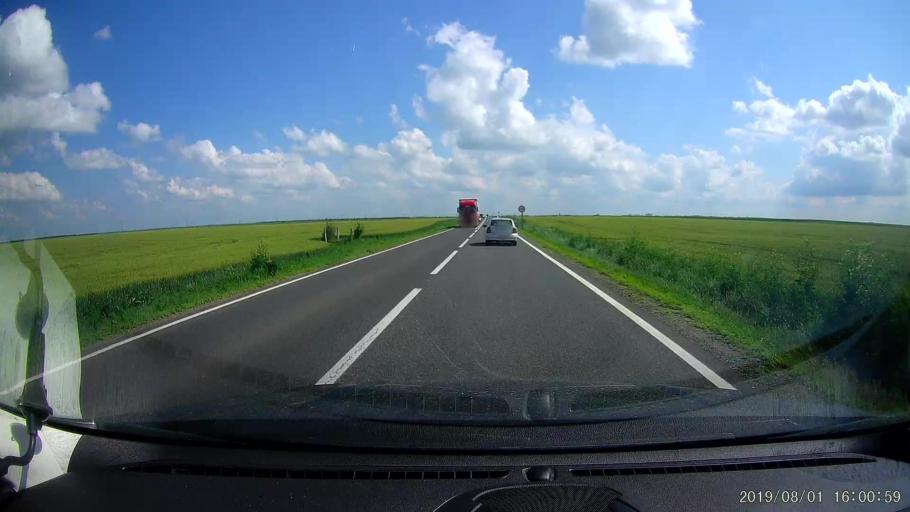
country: RO
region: Ialomita
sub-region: Comuna Ciulnita
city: Ciulnita
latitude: 44.5164
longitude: 27.3897
